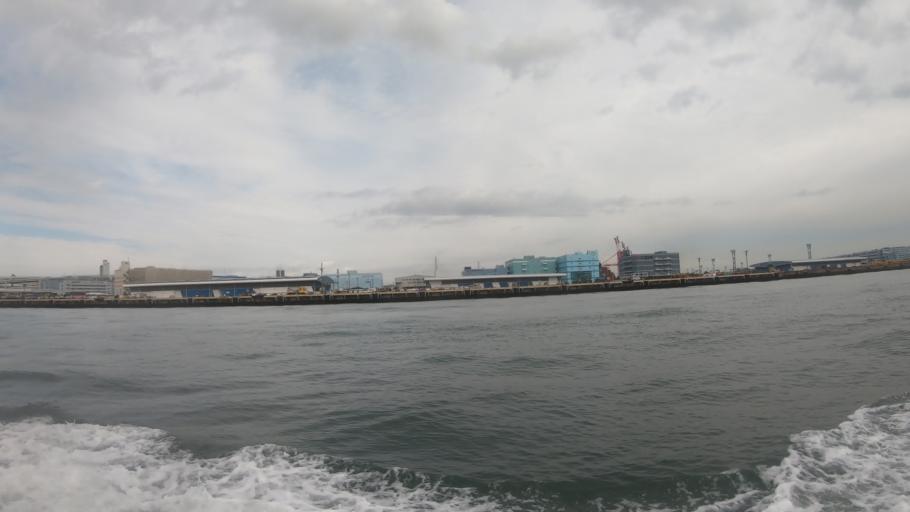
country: JP
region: Kanagawa
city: Yokohama
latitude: 35.4539
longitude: 139.6835
